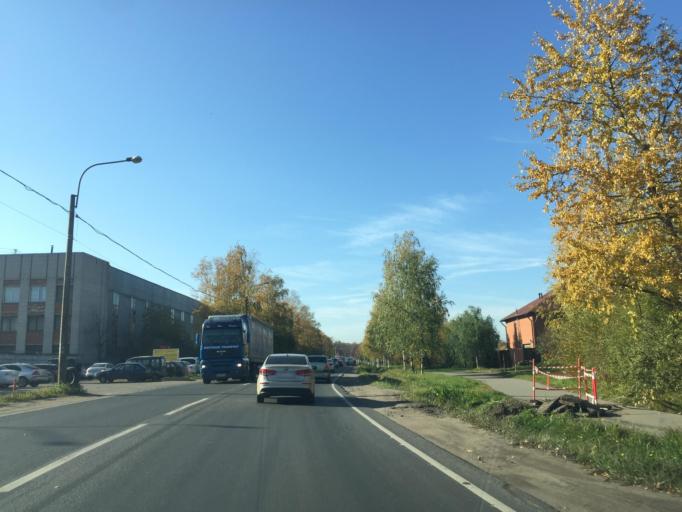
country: RU
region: St.-Petersburg
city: Tyarlevo
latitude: 59.7232
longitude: 30.4406
